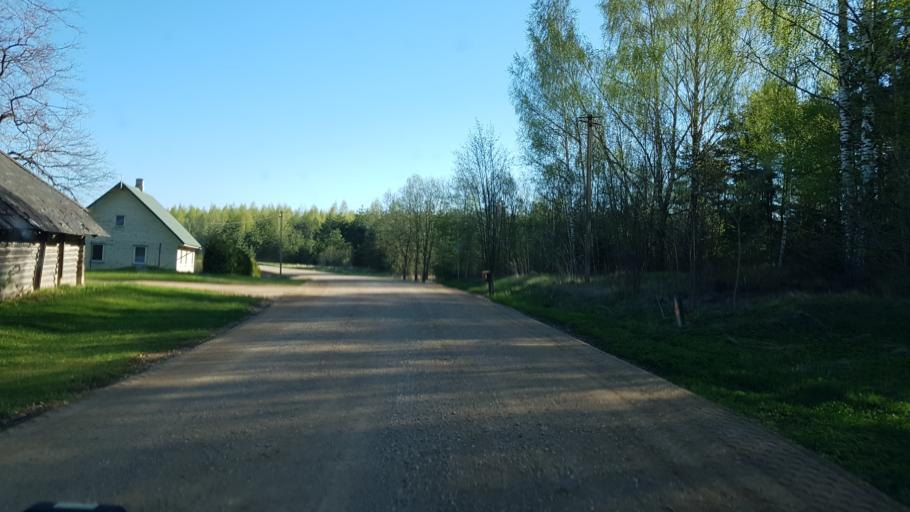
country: EE
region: Polvamaa
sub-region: Polva linn
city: Polva
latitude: 58.1085
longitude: 27.2386
